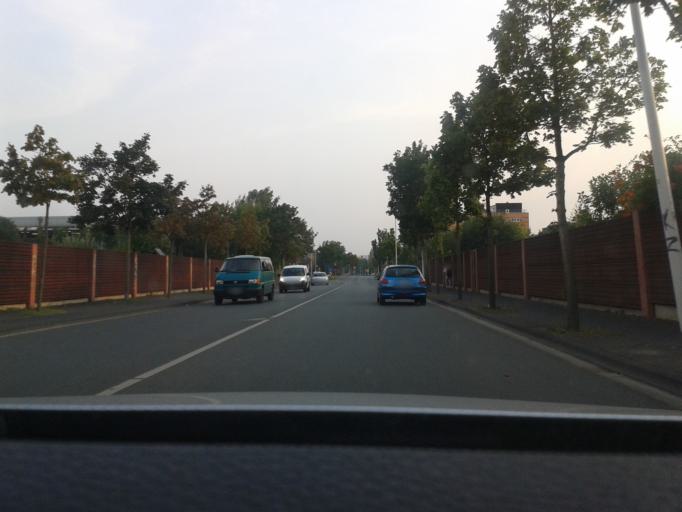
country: DE
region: Saxony
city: Albertstadt
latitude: 51.0317
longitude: 13.8042
